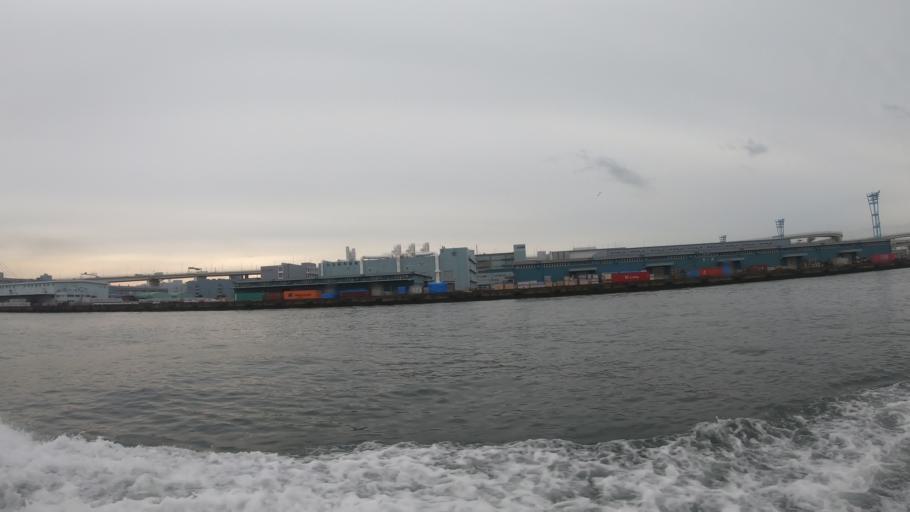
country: JP
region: Kanagawa
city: Yokohama
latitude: 35.4712
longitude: 139.6854
